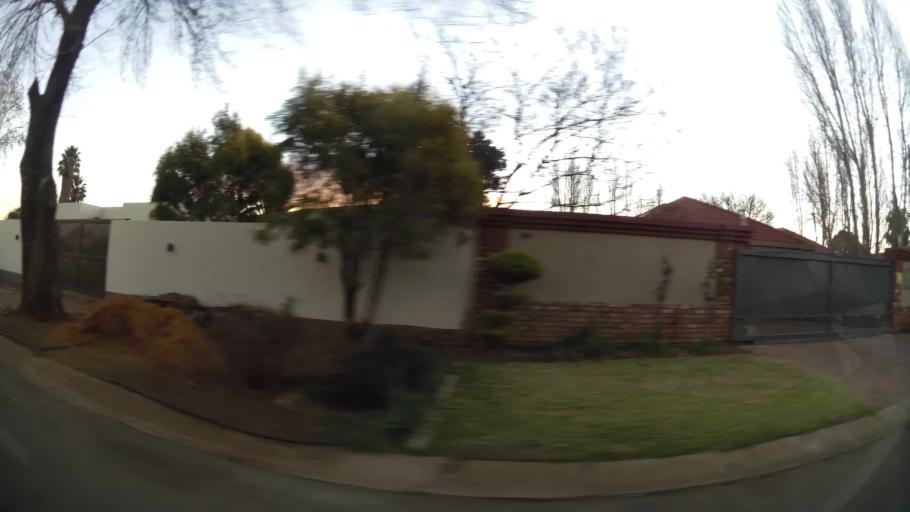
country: ZA
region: North-West
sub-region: Dr Kenneth Kaunda District Municipality
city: Potchefstroom
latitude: -26.7207
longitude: 27.1231
